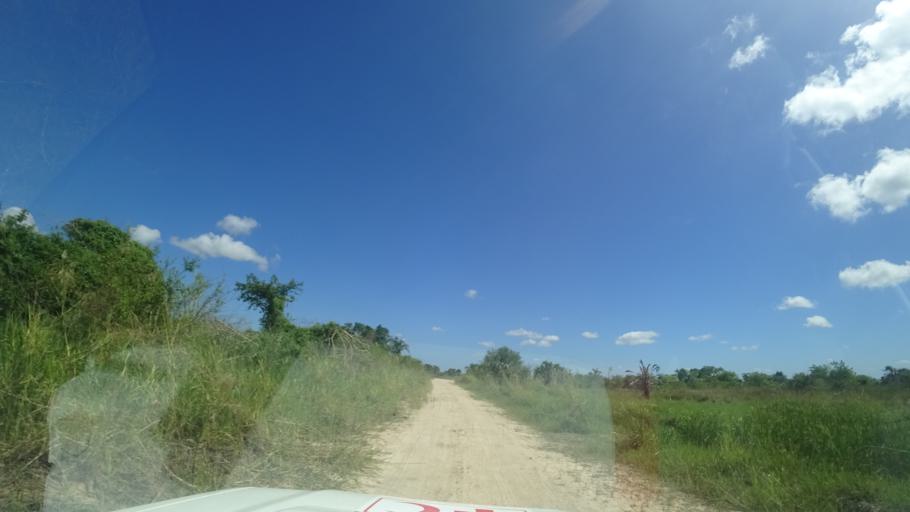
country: MZ
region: Sofala
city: Dondo
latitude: -19.3874
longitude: 34.5818
